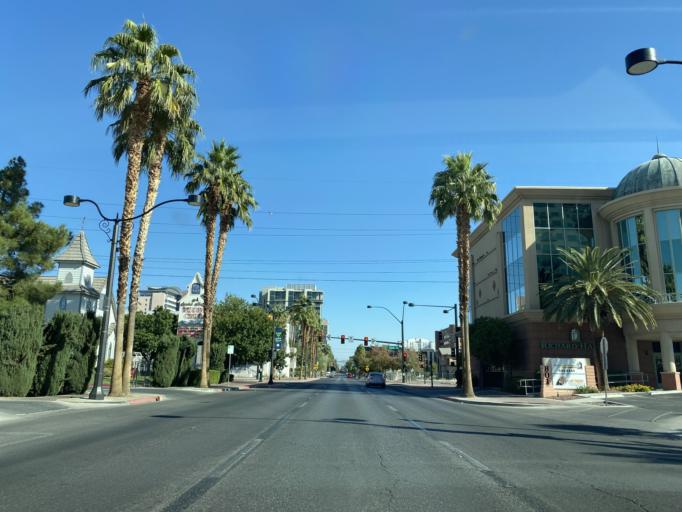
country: US
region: Nevada
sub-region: Clark County
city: Las Vegas
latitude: 36.1610
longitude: -115.1476
